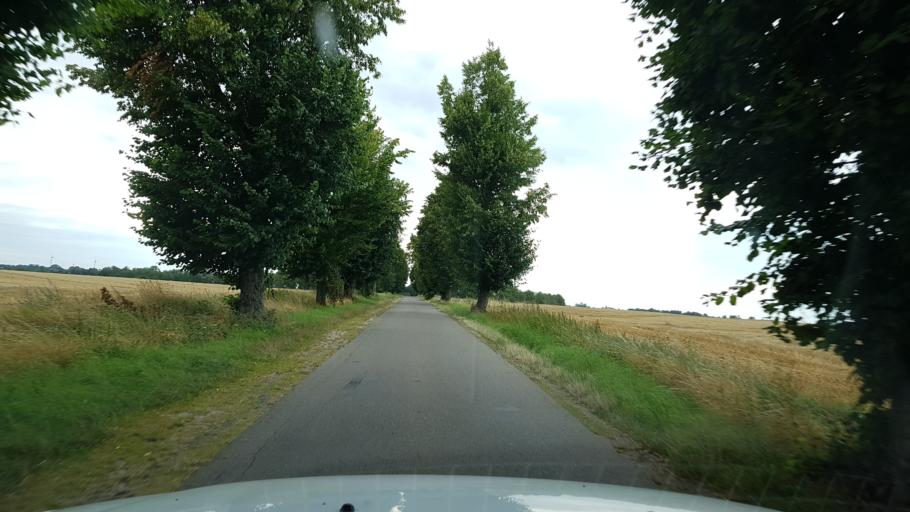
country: PL
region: West Pomeranian Voivodeship
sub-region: Powiat bialogardzki
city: Karlino
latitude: 54.1139
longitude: 15.8775
